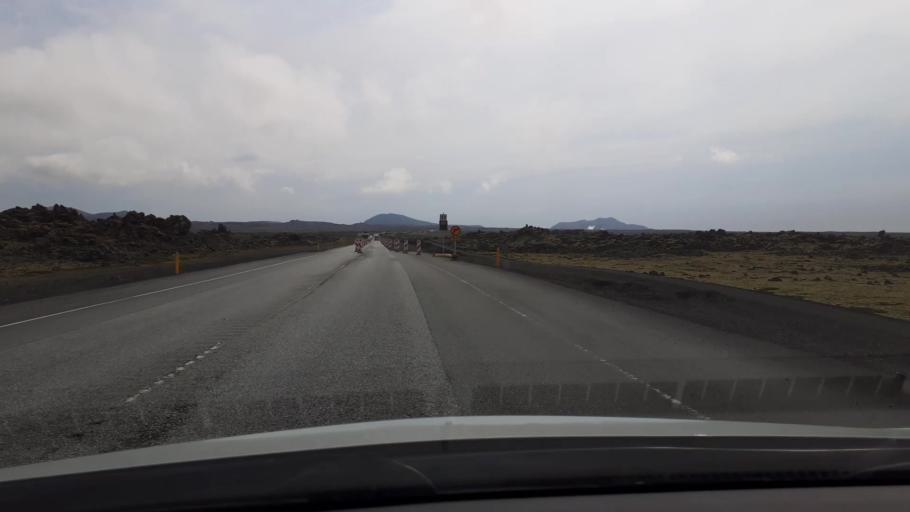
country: IS
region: Southern Peninsula
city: Vogar
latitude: 63.9296
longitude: -22.4260
